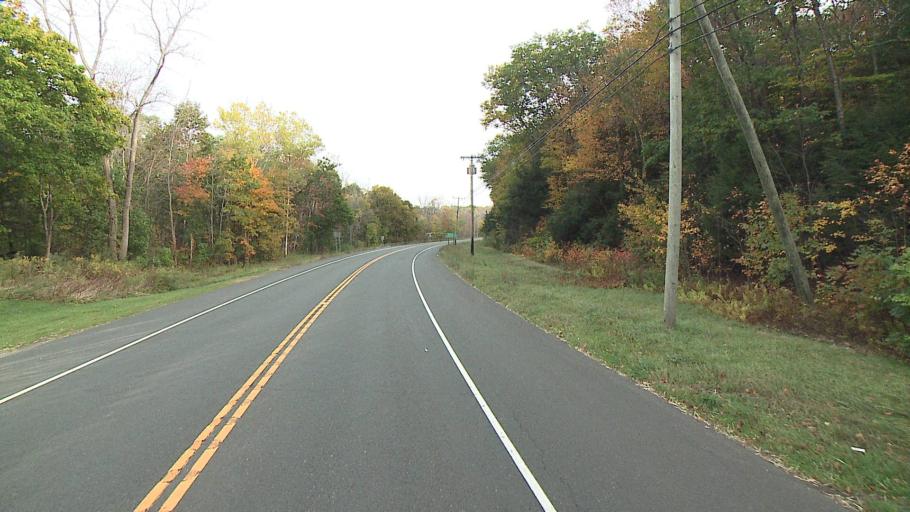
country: US
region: Connecticut
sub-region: Litchfield County
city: Winchester Center
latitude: 41.9884
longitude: -73.1715
